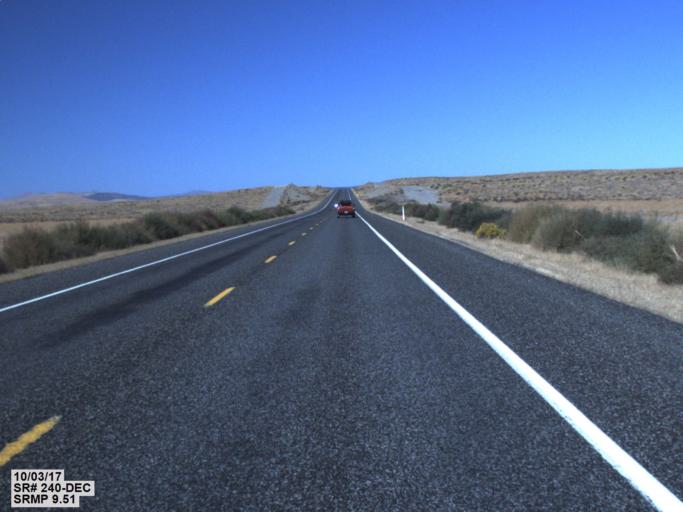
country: US
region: Washington
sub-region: Benton County
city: Benton City
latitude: 46.4896
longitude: -119.5895
